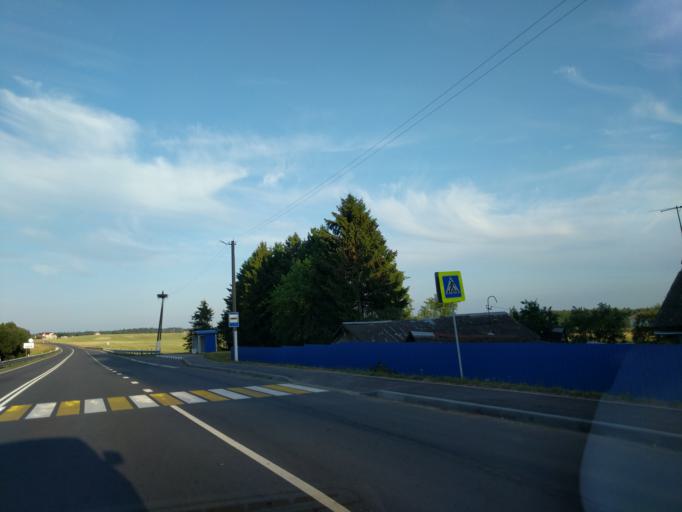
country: BY
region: Minsk
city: Syomkava
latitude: 54.1016
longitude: 27.4800
